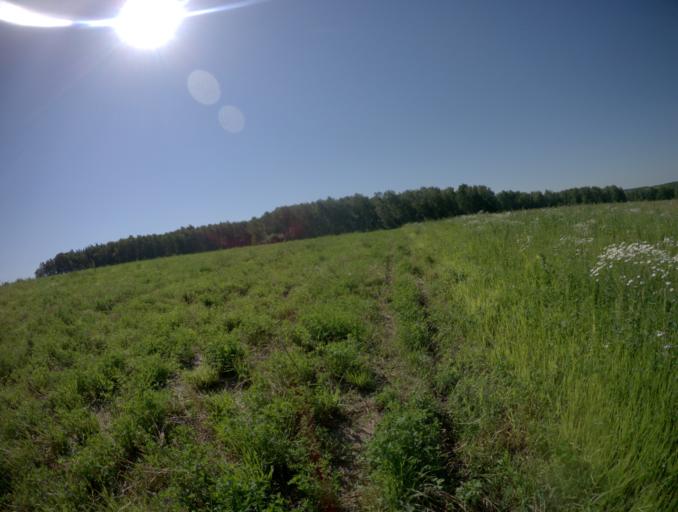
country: RU
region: Nizjnij Novgorod
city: Reshetikha
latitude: 56.1746
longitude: 43.3642
